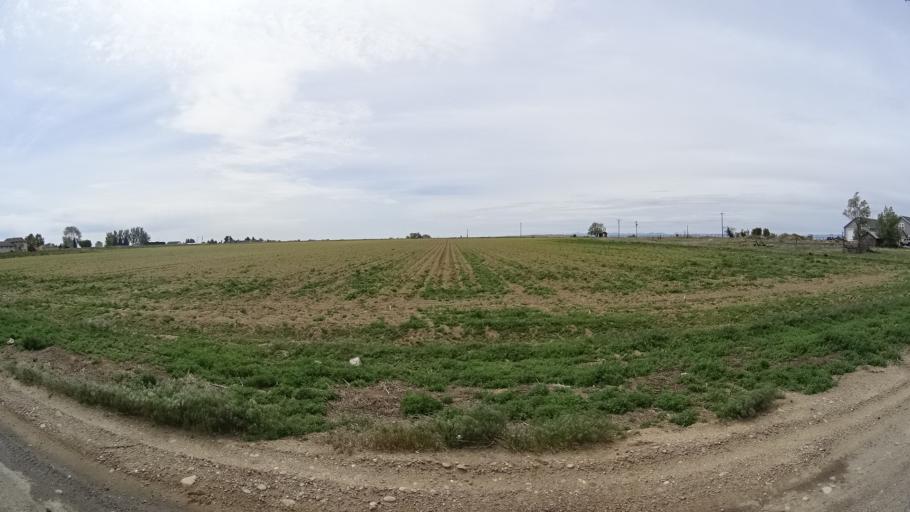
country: US
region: Idaho
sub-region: Ada County
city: Kuna
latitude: 43.5321
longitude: -116.4191
